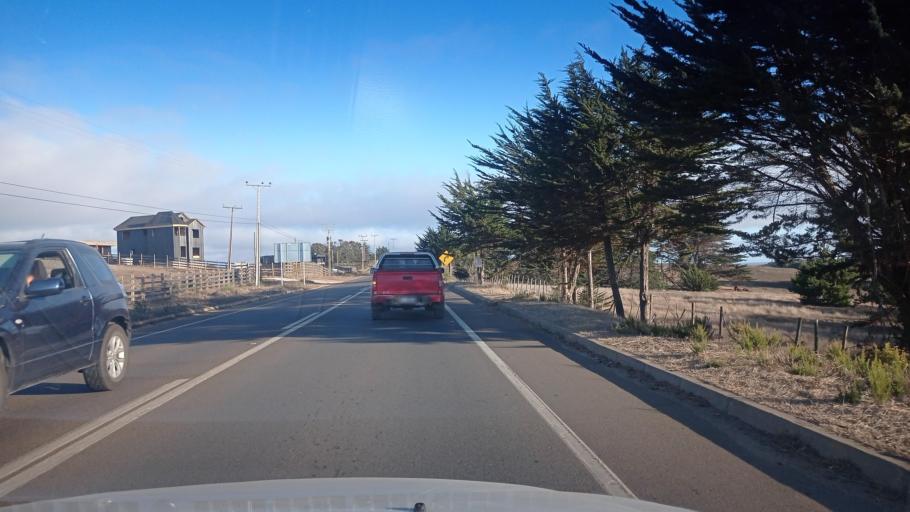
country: CL
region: O'Higgins
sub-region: Provincia de Colchagua
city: Santa Cruz
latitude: -34.4367
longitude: -72.0328
